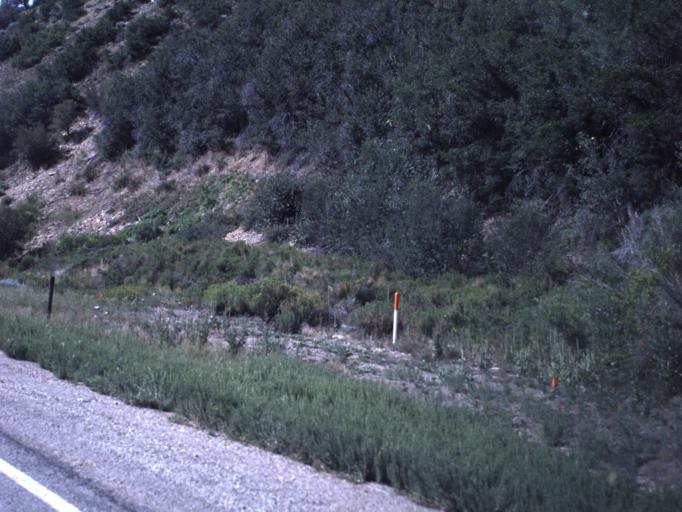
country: US
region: Utah
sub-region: Wasatch County
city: Heber
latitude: 40.3534
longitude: -111.2763
